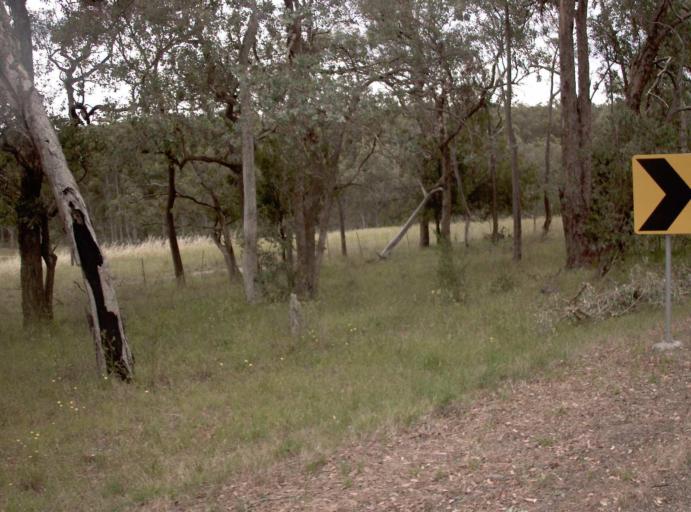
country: AU
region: Victoria
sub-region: East Gippsland
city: Bairnsdale
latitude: -37.7555
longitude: 147.3212
